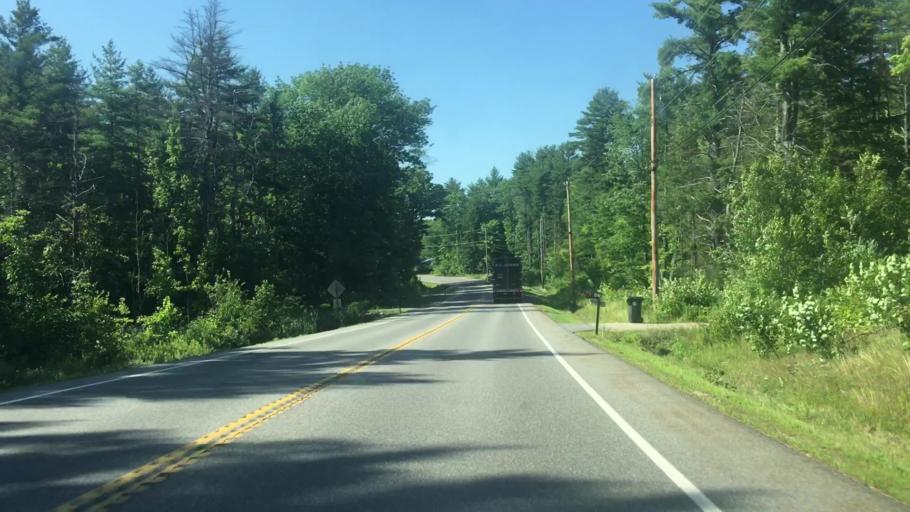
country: US
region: Maine
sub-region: York County
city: Buxton
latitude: 43.5725
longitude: -70.5124
